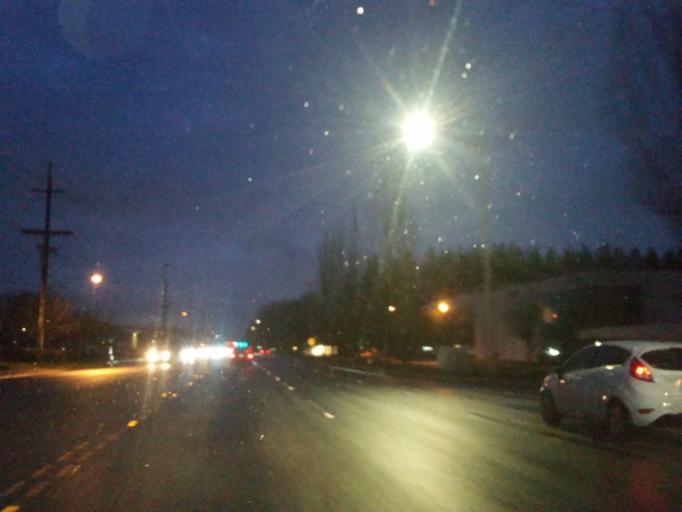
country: US
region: Washington
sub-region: King County
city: Kent
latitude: 47.4027
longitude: -122.2495
